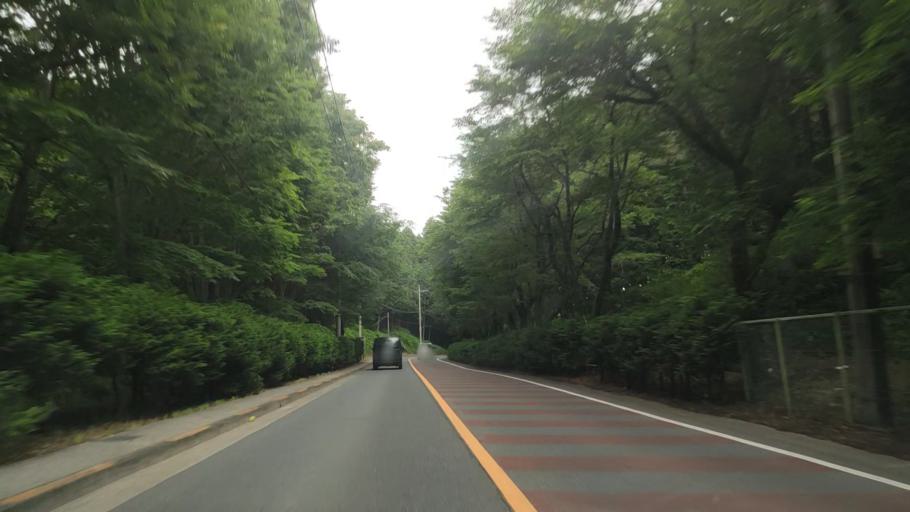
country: JP
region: Saitama
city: Hanno
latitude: 35.8126
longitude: 139.2993
